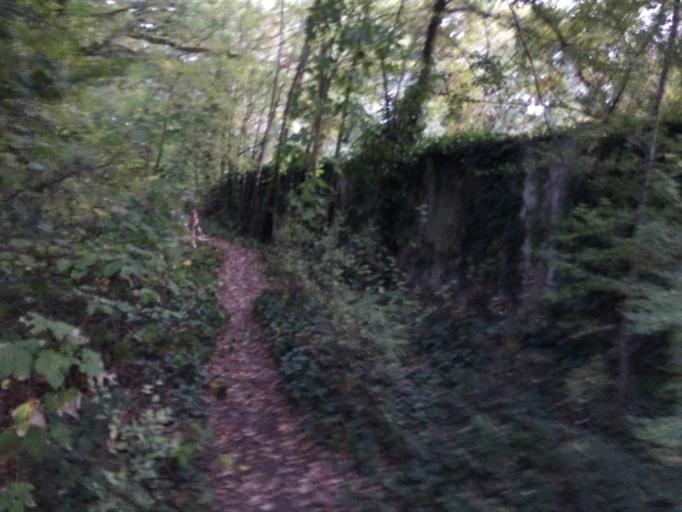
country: FR
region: Ile-de-France
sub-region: Departement des Yvelines
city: Velizy-Villacoublay
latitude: 48.7663
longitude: 2.1917
